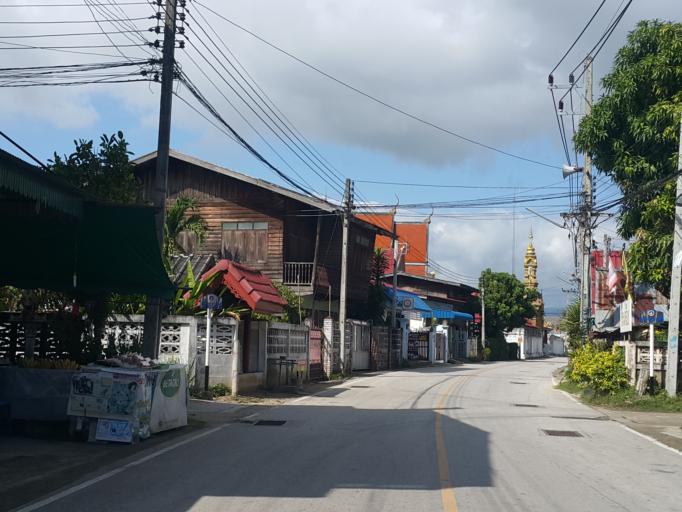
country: TH
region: Lampang
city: Hang Chat
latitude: 18.3252
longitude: 99.3472
